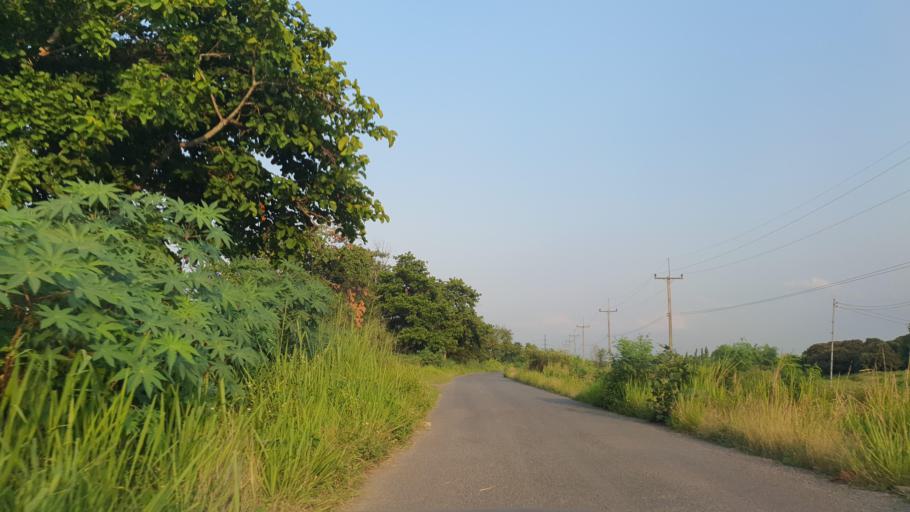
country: TH
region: Chiang Mai
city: Hang Dong
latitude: 18.6587
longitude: 98.9266
